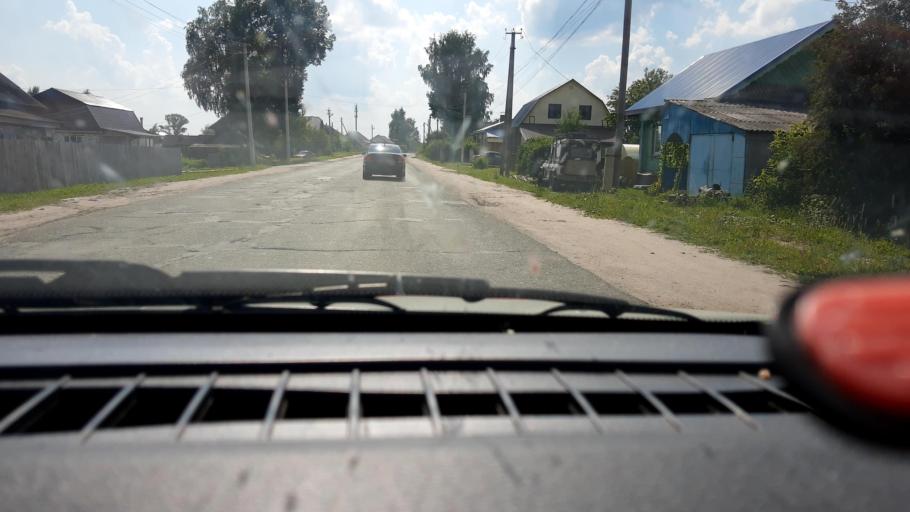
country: RU
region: Nizjnij Novgorod
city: Uren'
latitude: 57.4758
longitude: 45.8401
